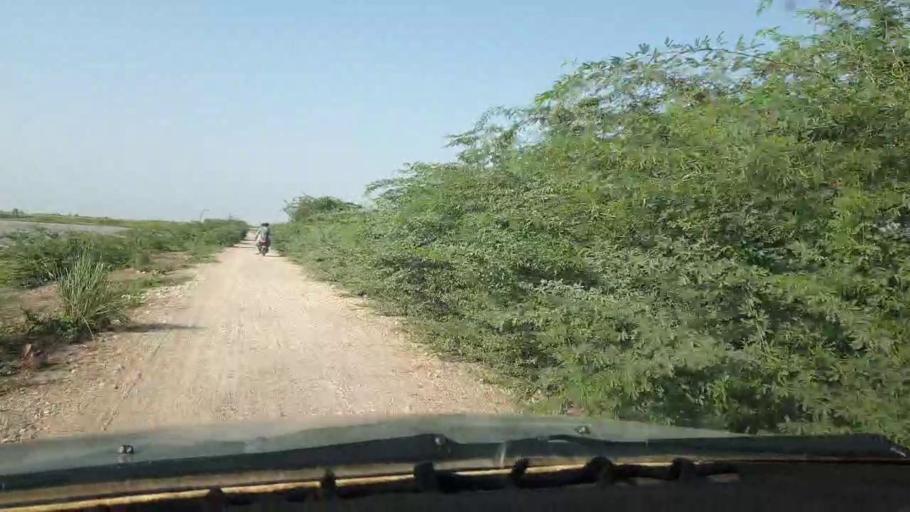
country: PK
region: Sindh
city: Chambar
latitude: 25.2737
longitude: 68.9234
